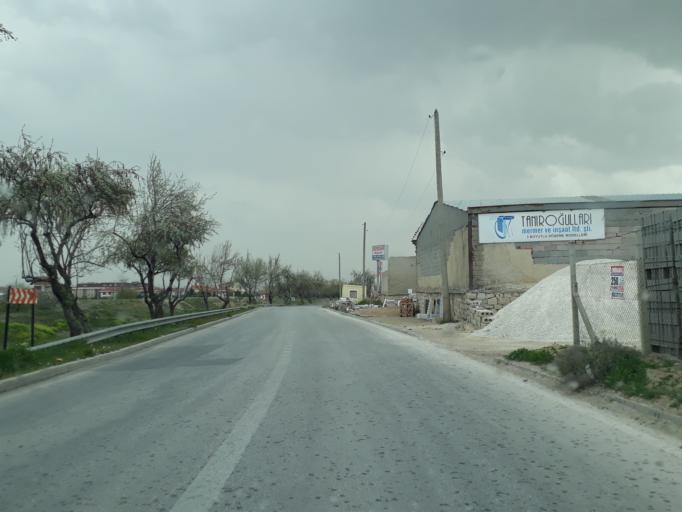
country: TR
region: Konya
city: Selcuklu
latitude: 37.9192
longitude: 32.4701
